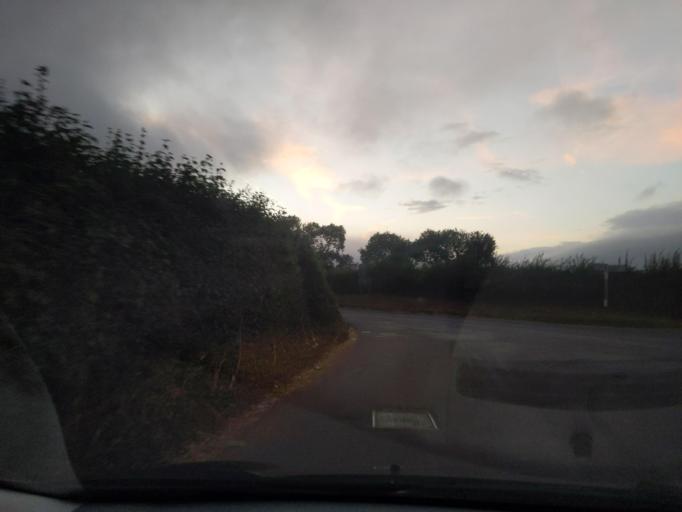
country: GB
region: England
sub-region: Devon
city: Ipplepen
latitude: 50.4849
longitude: -3.6186
